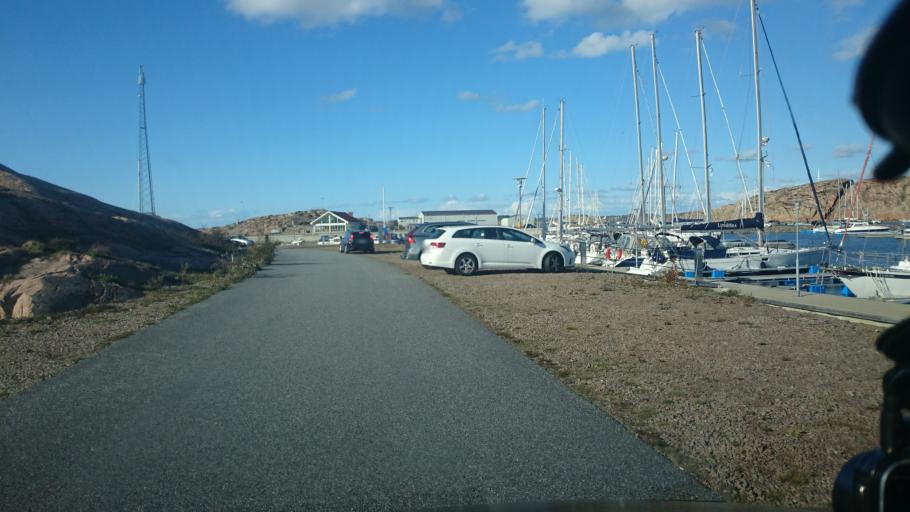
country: SE
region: Vaestra Goetaland
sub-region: Lysekils Kommun
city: Lysekil
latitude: 58.3136
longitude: 11.3964
